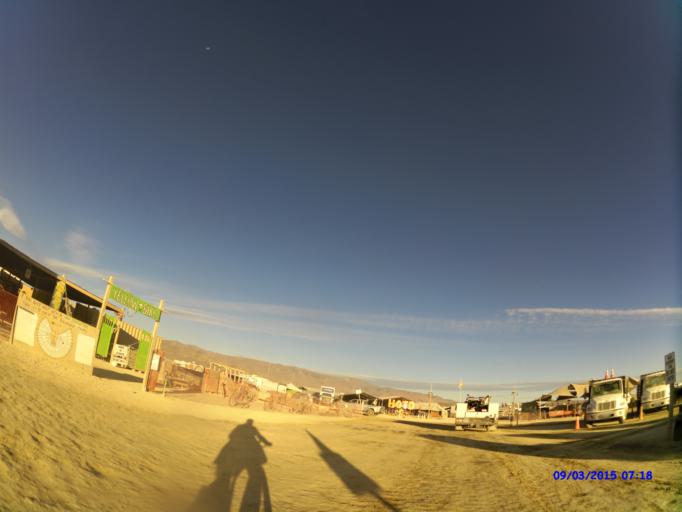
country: US
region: Nevada
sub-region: Pershing County
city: Lovelock
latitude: 40.7792
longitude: -119.2115
